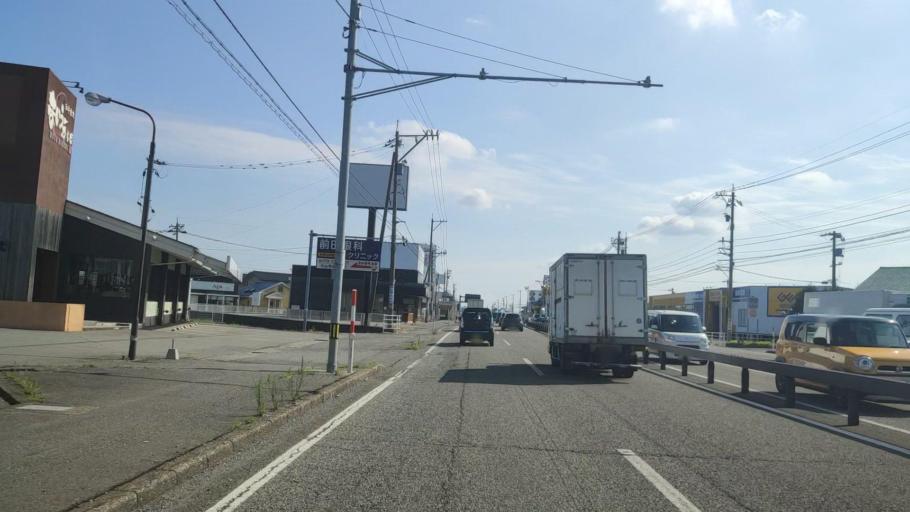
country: JP
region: Ishikawa
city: Matsuto
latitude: 36.5184
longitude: 136.5775
